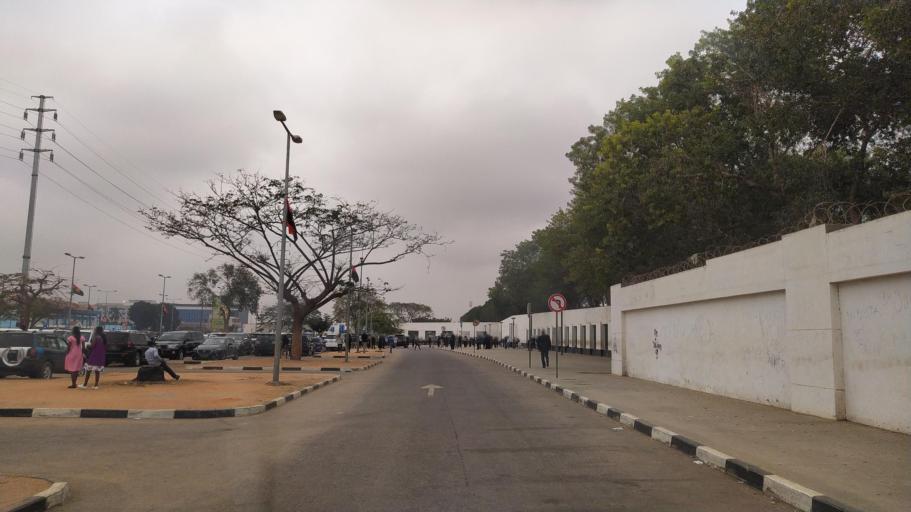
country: AO
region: Luanda
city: Luanda
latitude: -8.8399
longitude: 13.2648
